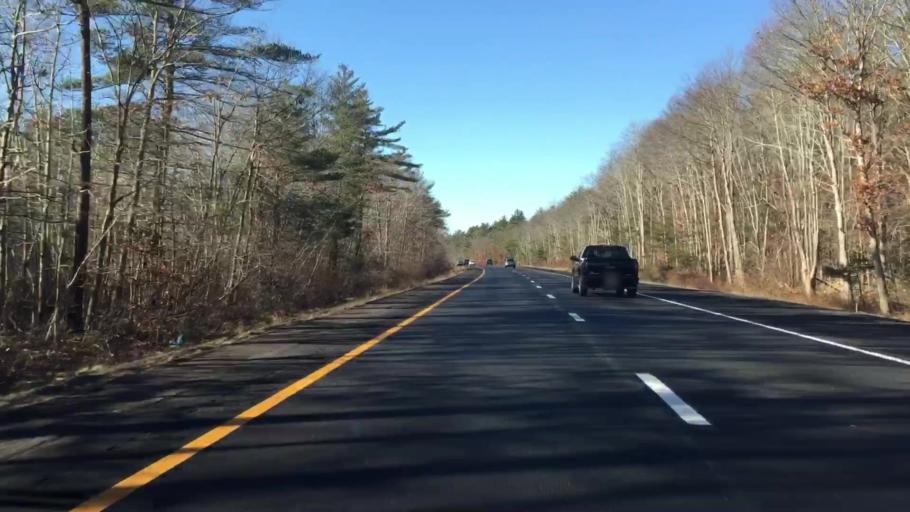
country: US
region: Massachusetts
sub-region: Plymouth County
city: Carver
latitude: 41.8429
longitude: -70.8344
